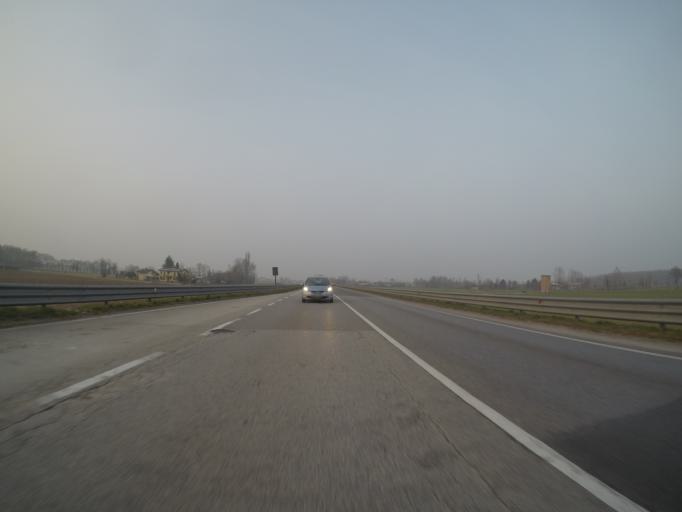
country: IT
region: Veneto
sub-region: Provincia di Padova
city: Loreggia
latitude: 45.5993
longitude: 11.9569
